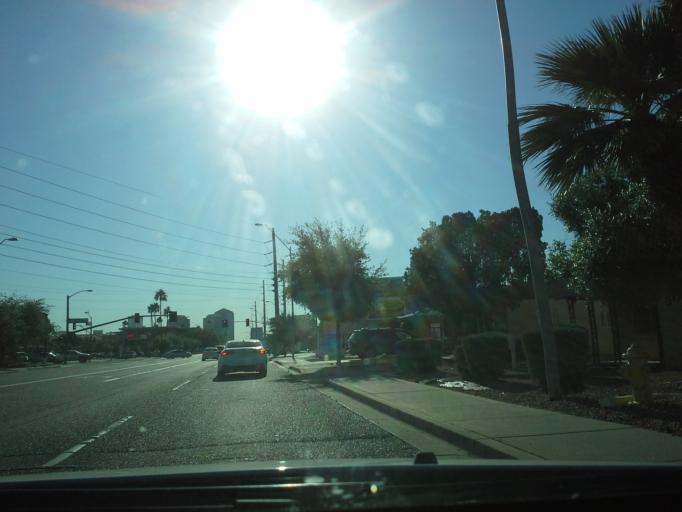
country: US
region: Arizona
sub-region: Maricopa County
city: Phoenix
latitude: 33.4804
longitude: -112.0926
